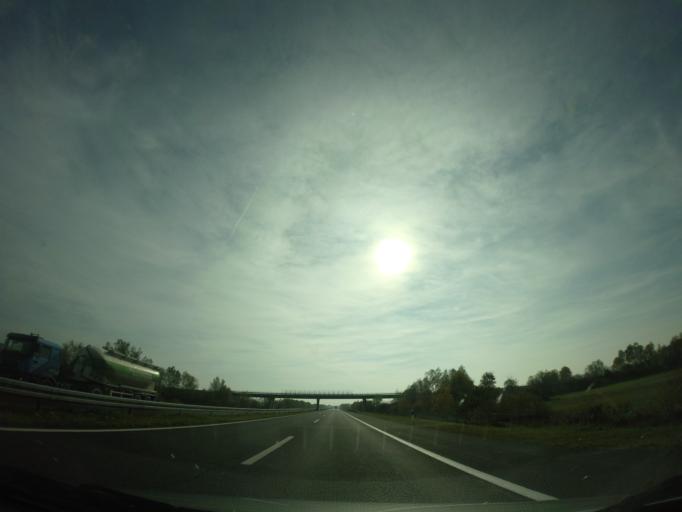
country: HR
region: Zagrebacka
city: Brckovljani
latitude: 45.9720
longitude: 16.2842
